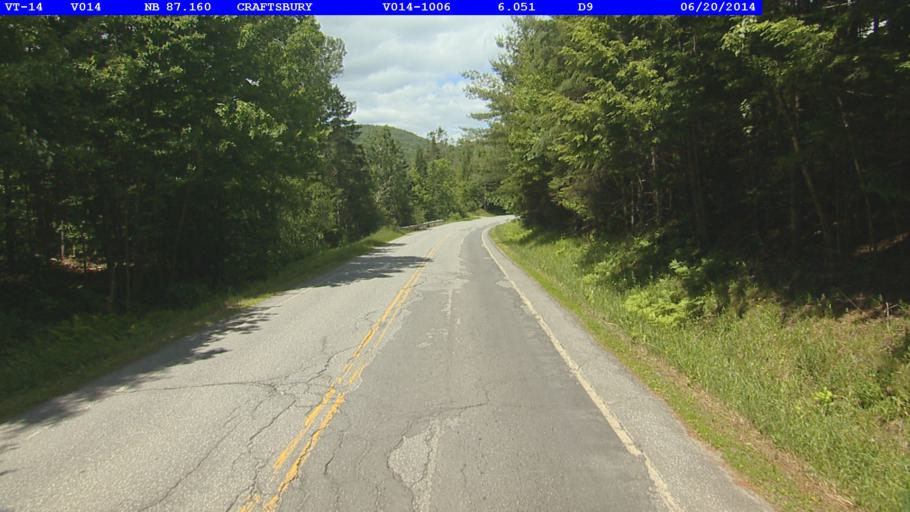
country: US
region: Vermont
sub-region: Caledonia County
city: Hardwick
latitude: 44.6777
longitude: -72.4045
